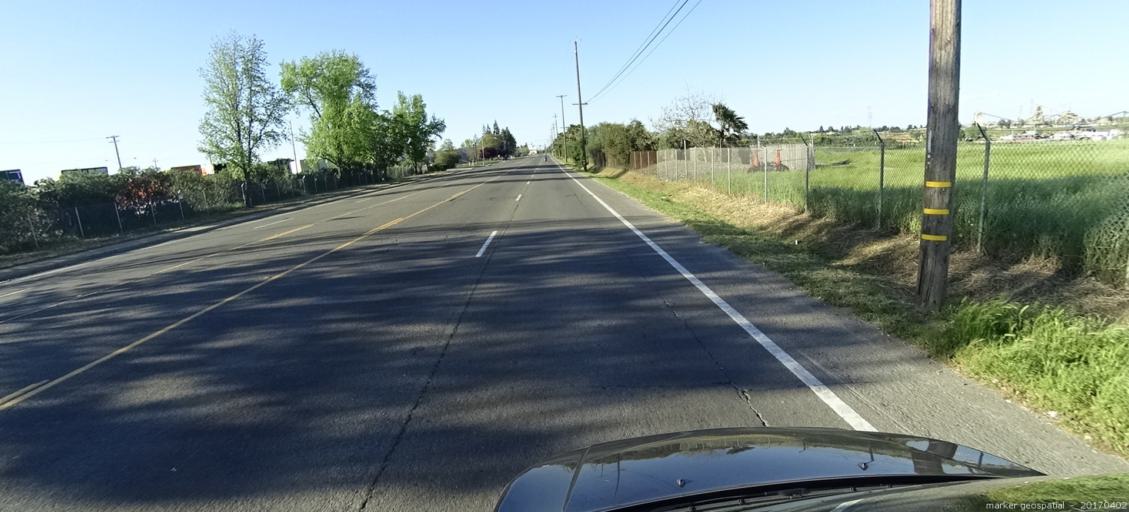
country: US
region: California
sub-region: Sacramento County
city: Rosemont
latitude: 38.5352
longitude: -121.3907
